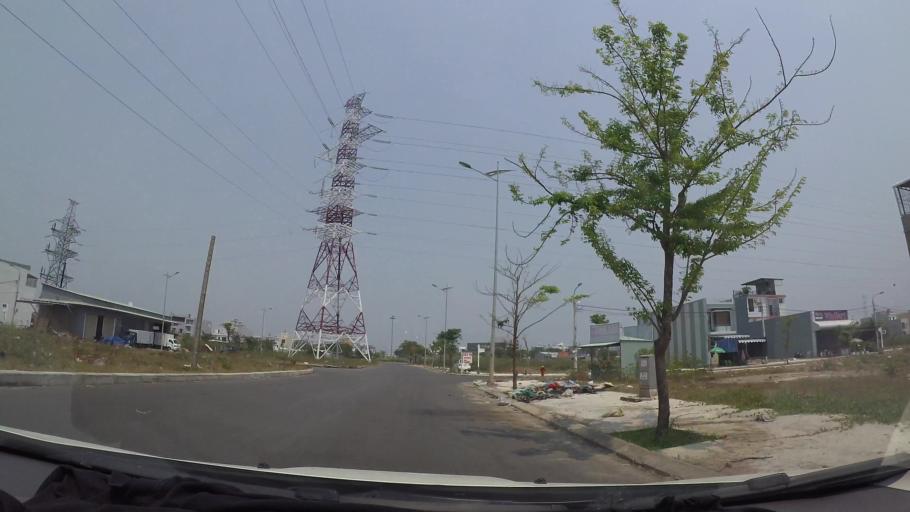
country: VN
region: Da Nang
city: Ngu Hanh Son
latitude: 16.0170
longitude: 108.2291
